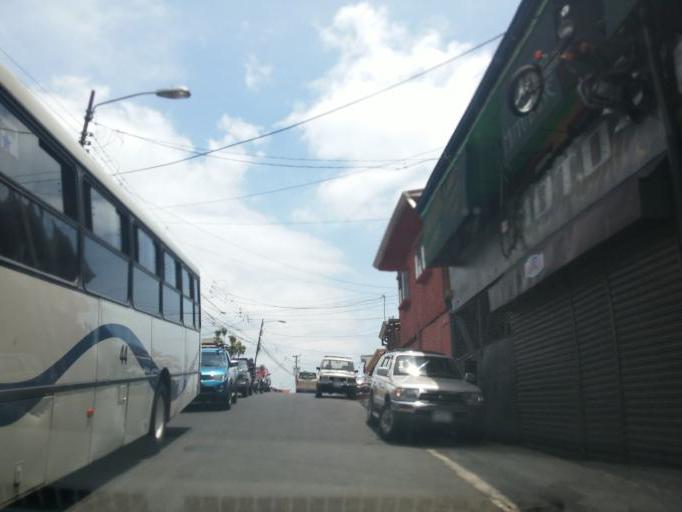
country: CR
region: San Jose
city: Alajuelita
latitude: 9.9058
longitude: -84.0804
